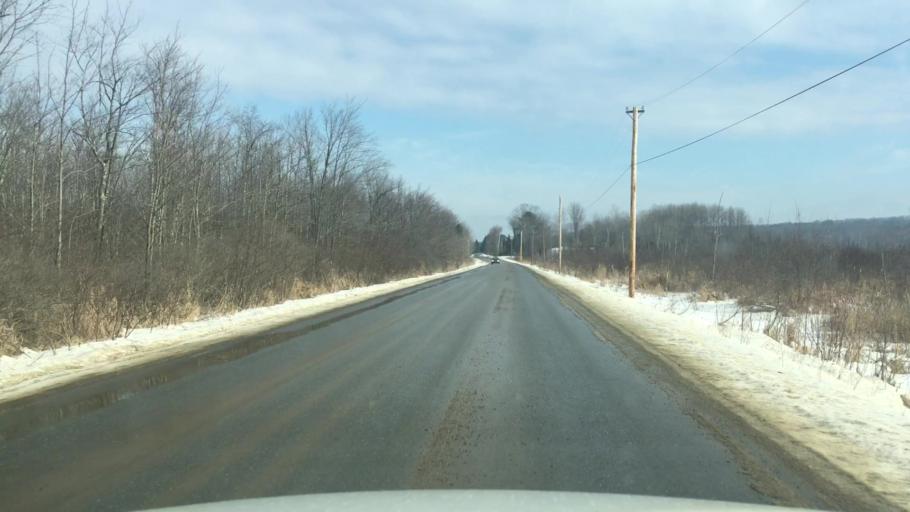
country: US
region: Maine
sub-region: Penobscot County
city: Hermon
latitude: 44.7588
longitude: -68.9634
